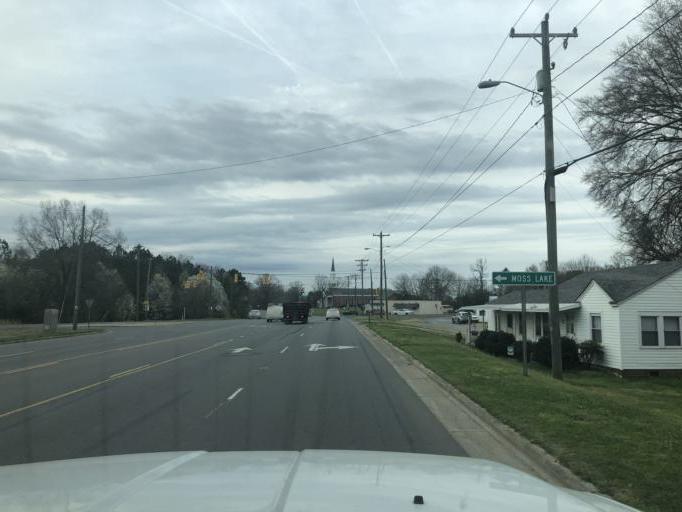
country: US
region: North Carolina
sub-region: Cleveland County
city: Shelby
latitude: 35.2926
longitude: -81.4900
